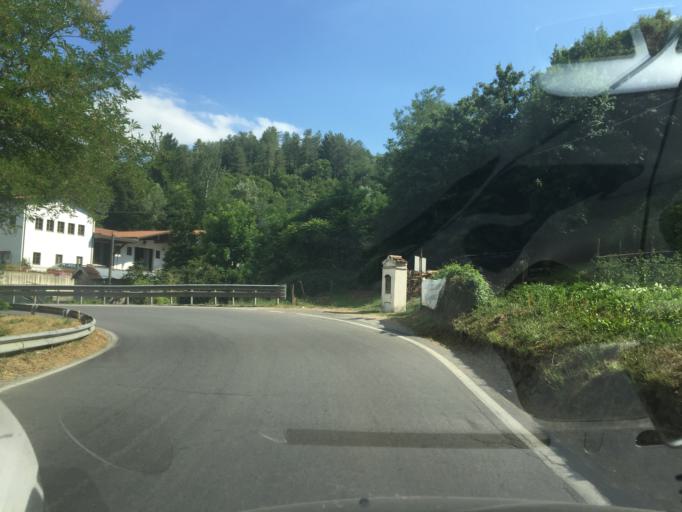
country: IT
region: Tuscany
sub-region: Provincia di Lucca
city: Pieve Fosciana
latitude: 44.1293
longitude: 10.3775
